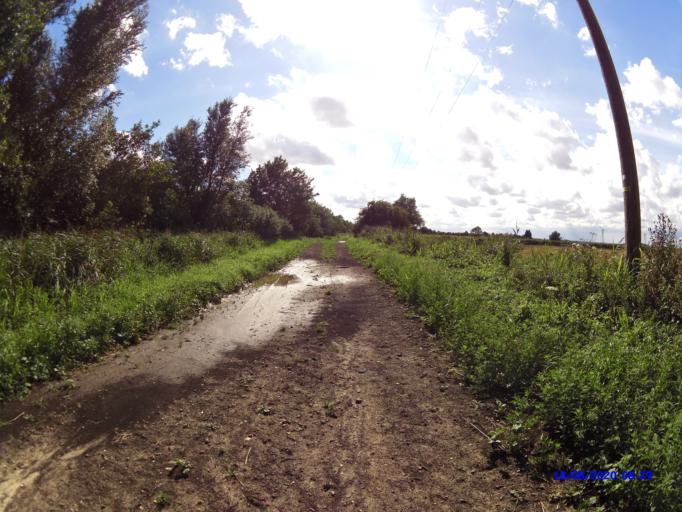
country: GB
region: England
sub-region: Cambridgeshire
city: Ramsey
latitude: 52.5011
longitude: -0.0804
